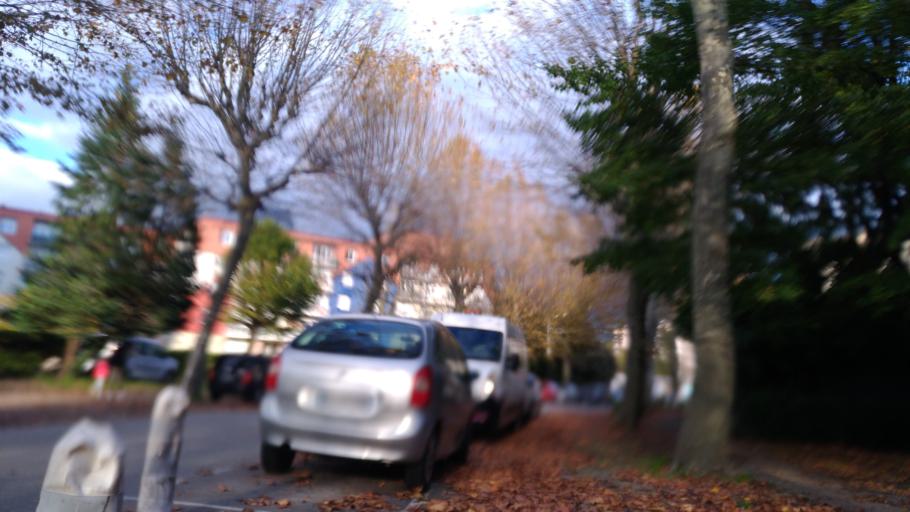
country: FR
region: Rhone-Alpes
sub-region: Departement de l'Isere
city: Fontaine
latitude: 45.1951
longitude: 5.6876
